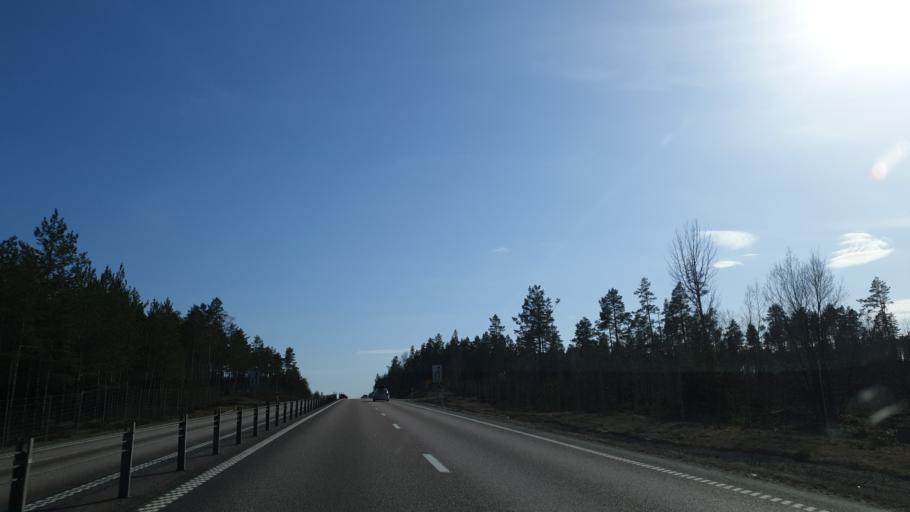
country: SE
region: Gaevleborg
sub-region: Hudiksvalls Kommun
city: Hudiksvall
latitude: 61.8552
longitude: 17.2045
